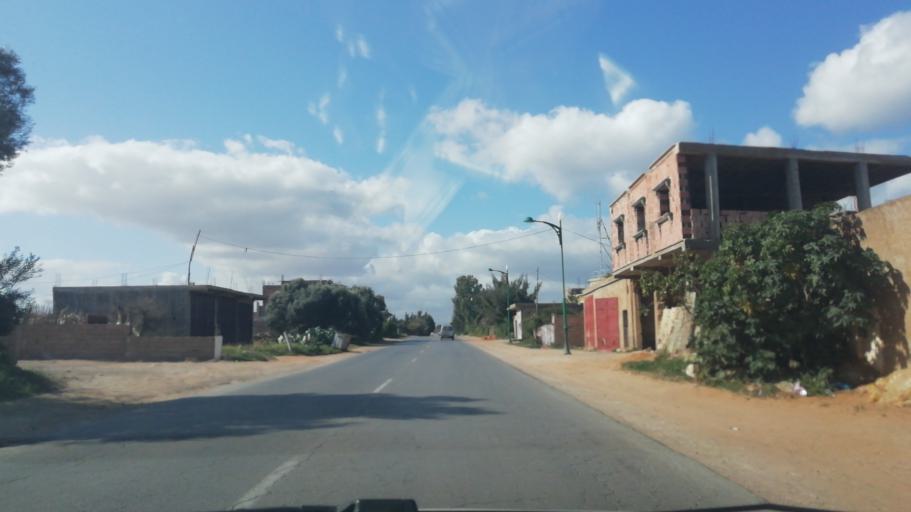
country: DZ
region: Relizane
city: Mazouna
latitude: 36.2817
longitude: 0.6416
